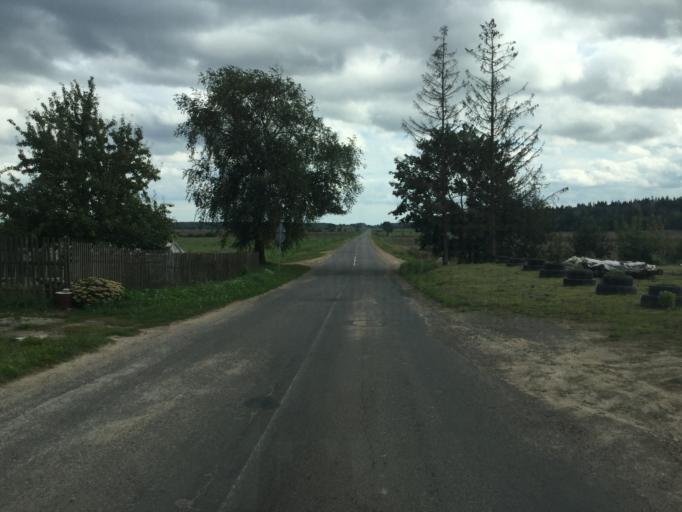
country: BY
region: Vitebsk
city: Vitebsk
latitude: 55.1432
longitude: 30.2870
